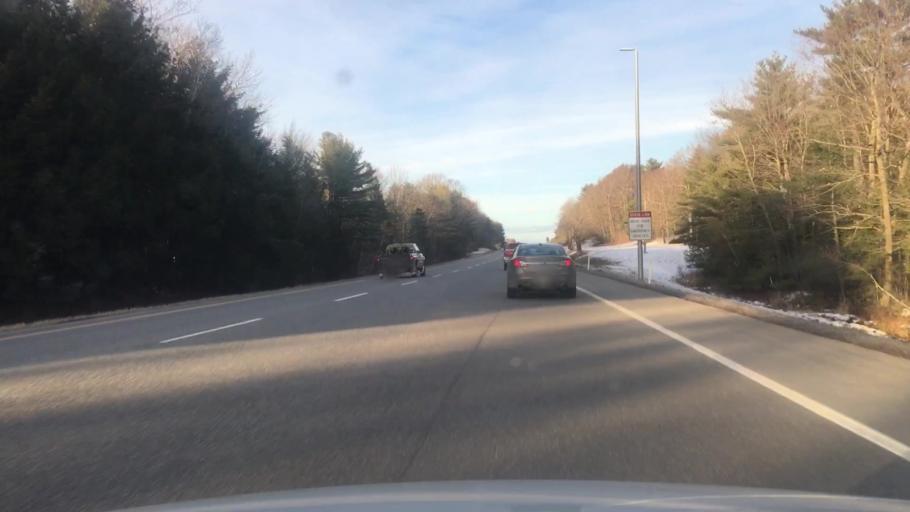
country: US
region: Maine
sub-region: Kennebec County
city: Augusta
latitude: 44.3581
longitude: -69.7797
